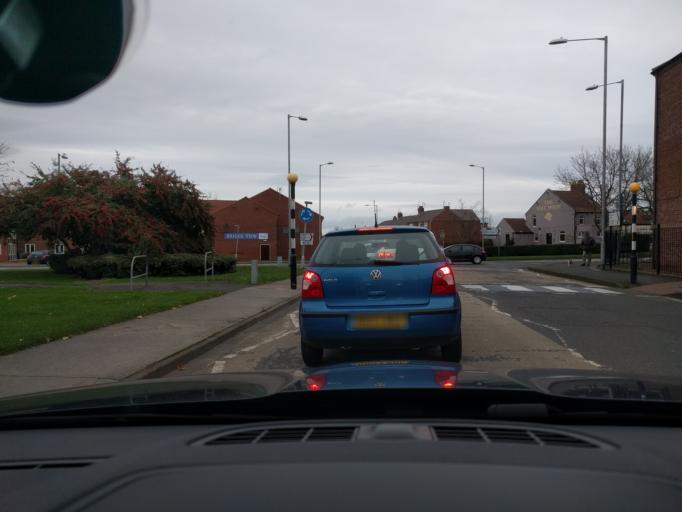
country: GB
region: England
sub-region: Northumberland
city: Ashington
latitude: 55.1645
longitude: -1.5802
